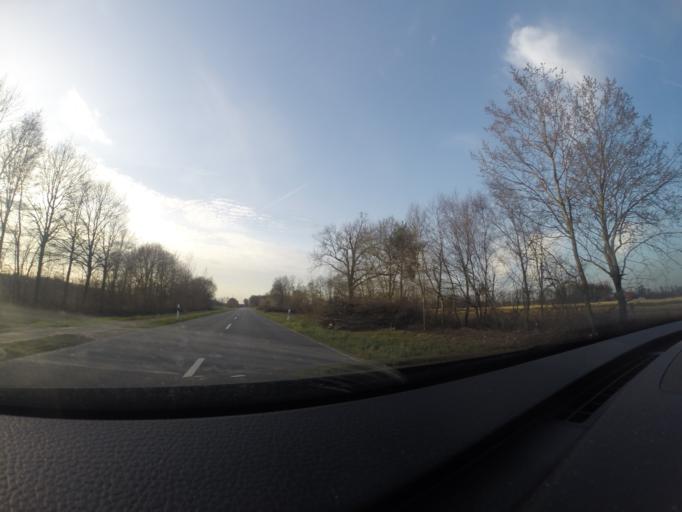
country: DE
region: North Rhine-Westphalia
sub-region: Regierungsbezirk Munster
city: Ahaus
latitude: 52.1140
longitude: 6.9451
